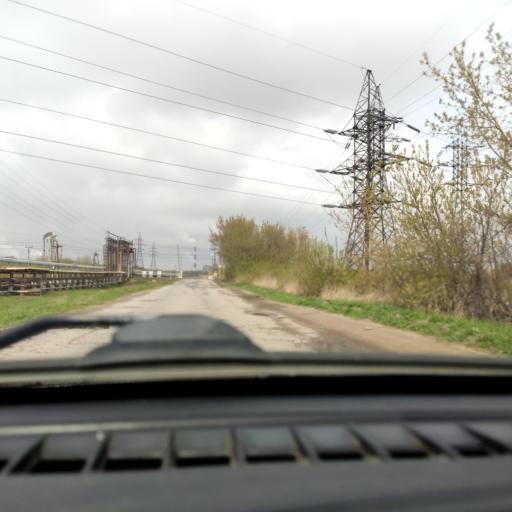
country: RU
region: Samara
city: Zhigulevsk
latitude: 53.5391
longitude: 49.4942
